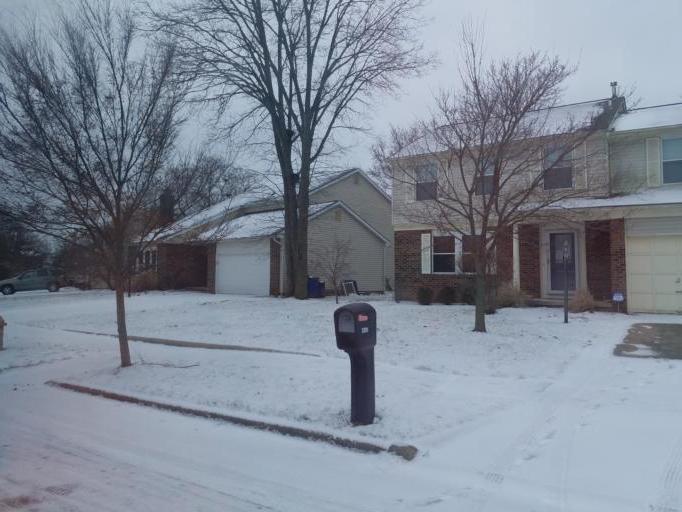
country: US
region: Ohio
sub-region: Delaware County
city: Powell
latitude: 40.1225
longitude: -83.0755
